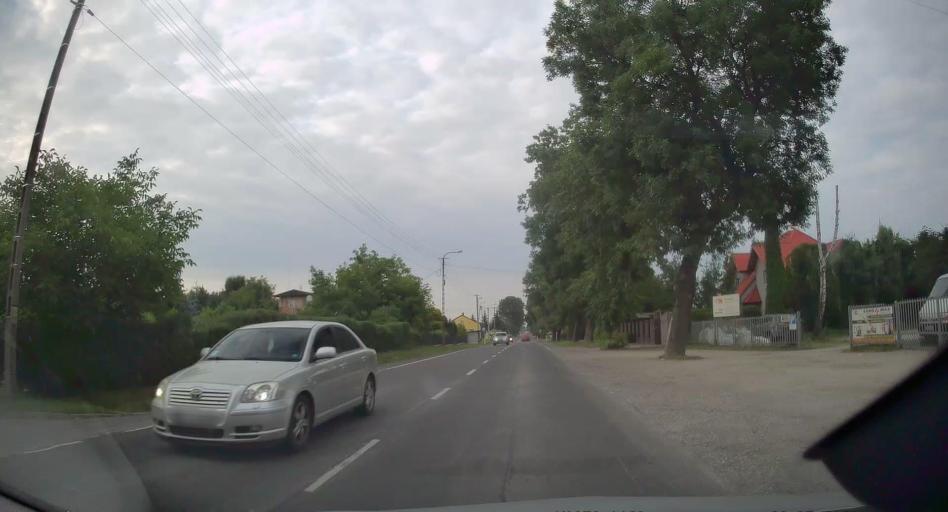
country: PL
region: Lodz Voivodeship
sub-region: Powiat radomszczanski
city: Radomsko
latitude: 51.1016
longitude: 19.4626
